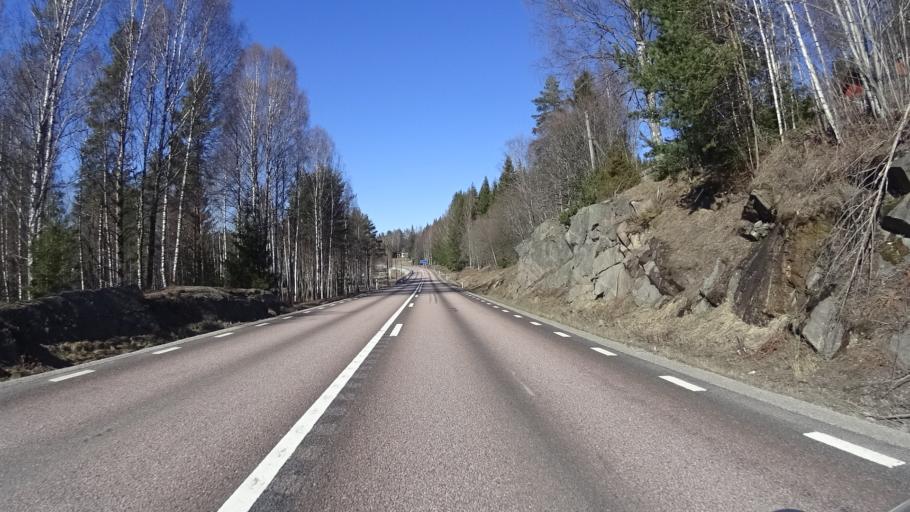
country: SE
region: Vaermland
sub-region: Sunne Kommun
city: Sunne
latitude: 59.6480
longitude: 12.9449
